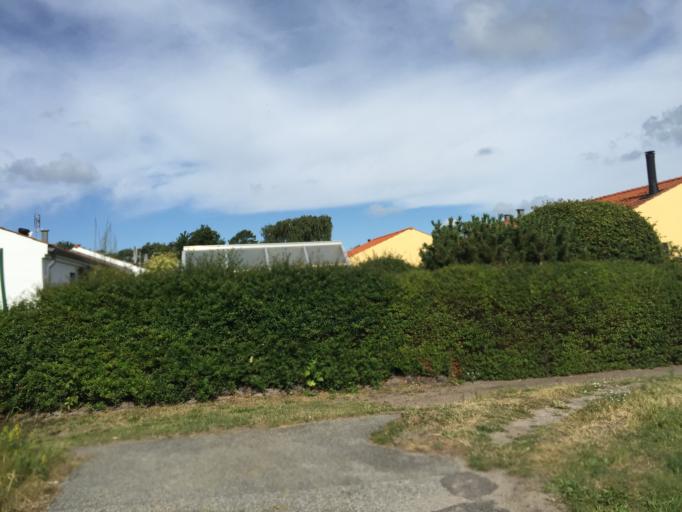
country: SE
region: Skane
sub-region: Vellinge Kommun
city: Skanor med Falsterbo
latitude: 55.3958
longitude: 12.8456
